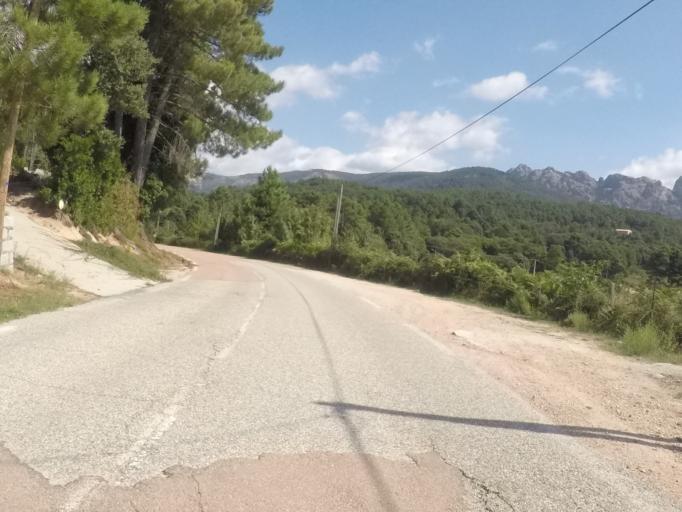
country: FR
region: Corsica
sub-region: Departement de la Corse-du-Sud
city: Zonza
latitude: 41.7583
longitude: 9.1827
